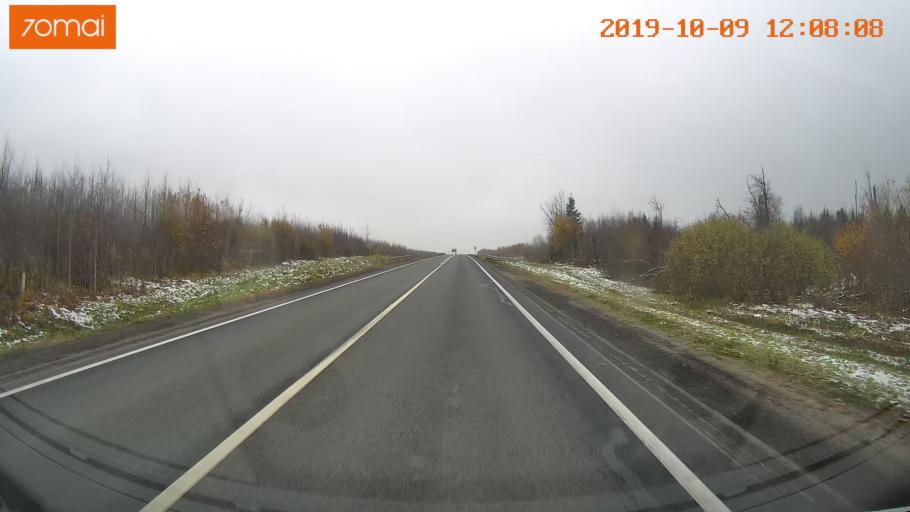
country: RU
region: Jaroslavl
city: Prechistoye
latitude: 58.5906
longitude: 40.3461
